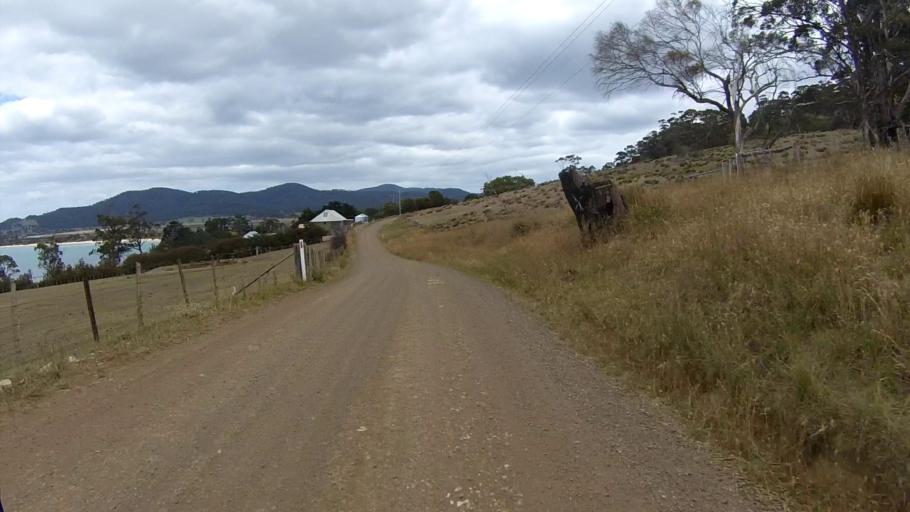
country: AU
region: Tasmania
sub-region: Sorell
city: Sorell
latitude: -42.6262
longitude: 147.9323
